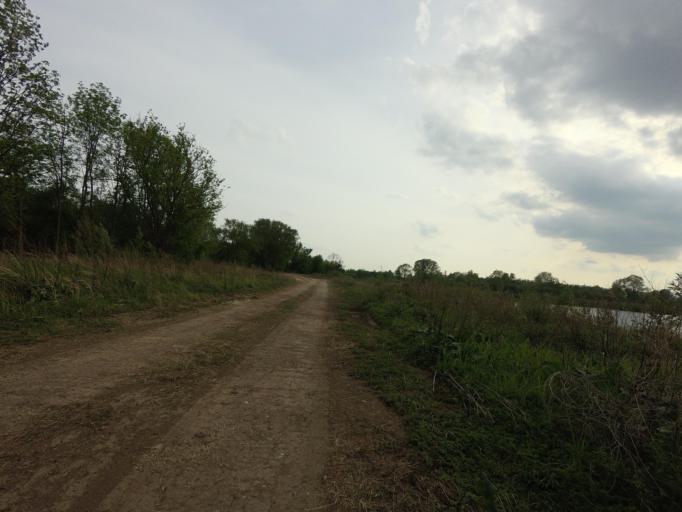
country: DE
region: Lower Saxony
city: Nordstemmen
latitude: 52.1614
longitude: 9.7610
